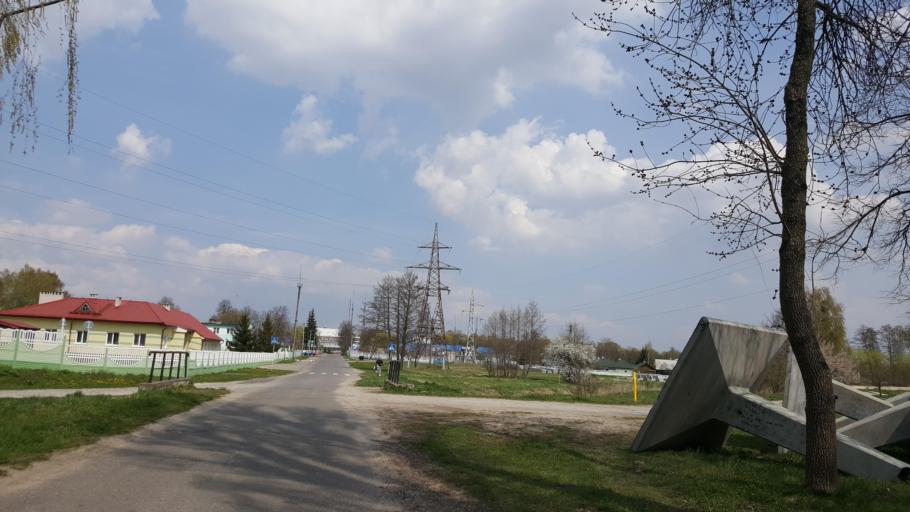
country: BY
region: Brest
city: Zhabinka
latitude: 52.1909
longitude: 24.0168
